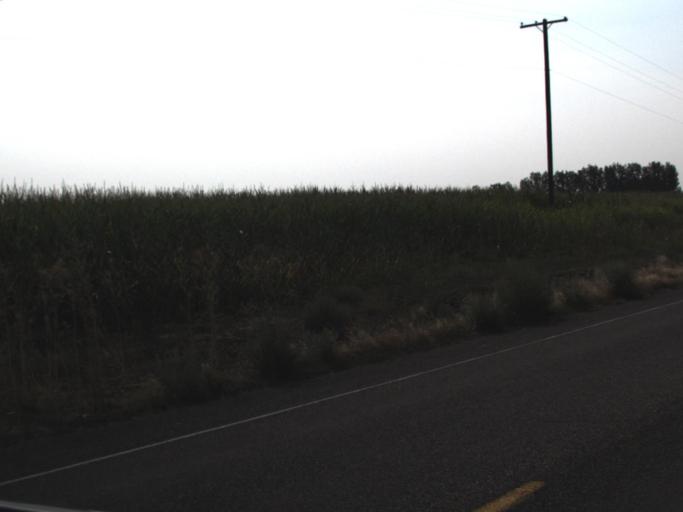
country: US
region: Washington
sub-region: Yakima County
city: Mabton
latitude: 46.2235
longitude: -120.0482
